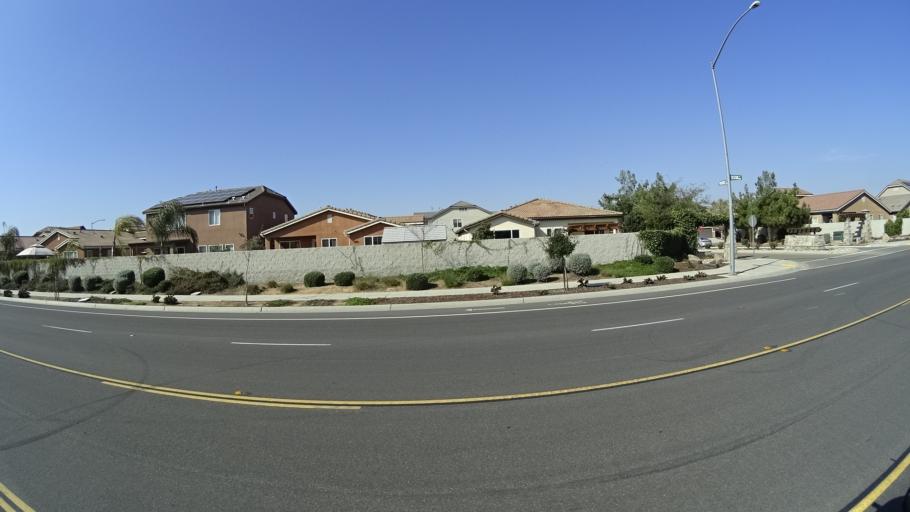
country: US
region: California
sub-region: Fresno County
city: Clovis
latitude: 36.8901
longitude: -119.7387
